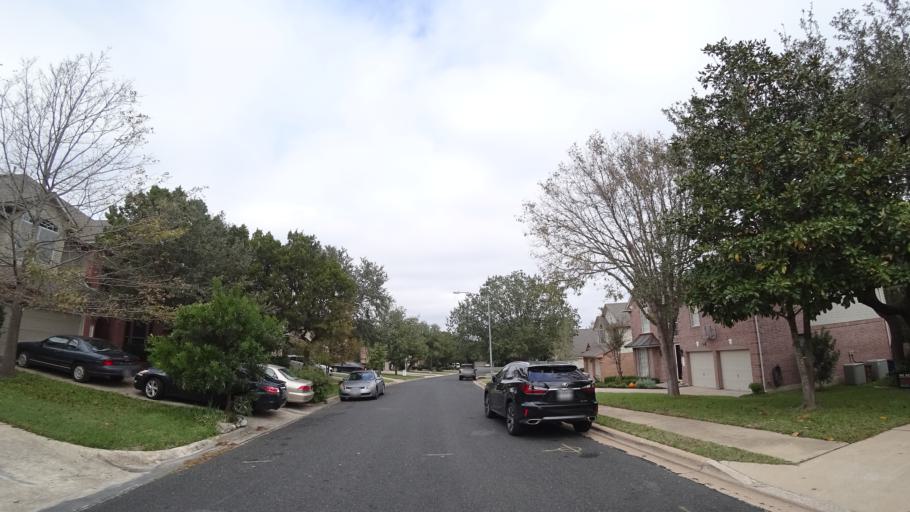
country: US
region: Texas
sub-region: Travis County
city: Shady Hollow
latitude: 30.2215
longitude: -97.8759
